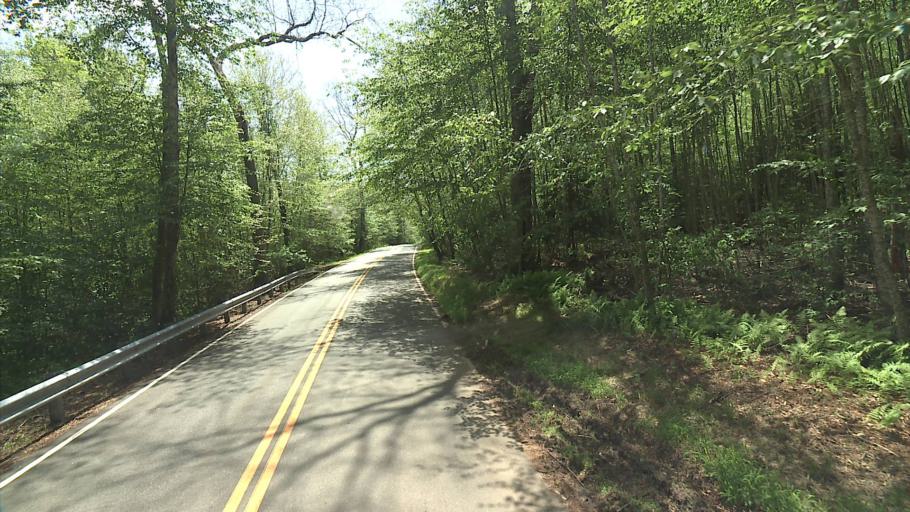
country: US
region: Connecticut
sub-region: New London County
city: Colchester
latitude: 41.4603
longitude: -72.3359
